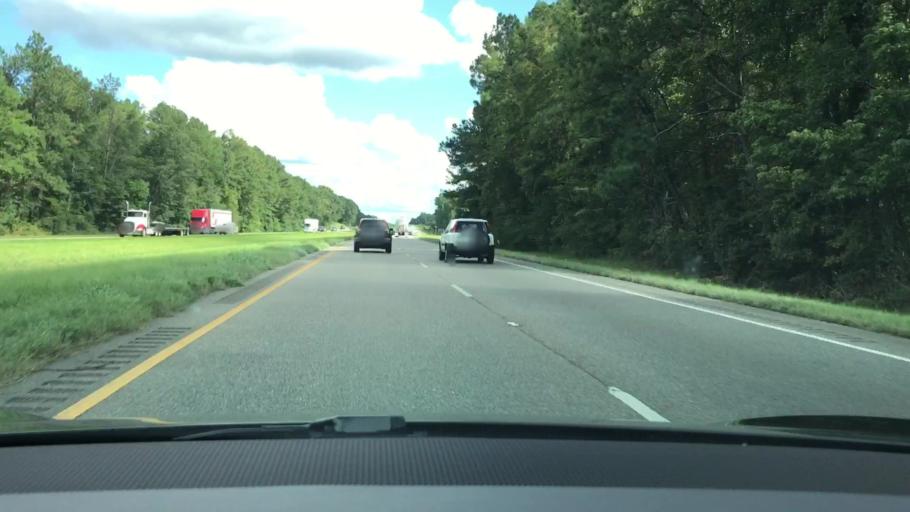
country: US
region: Alabama
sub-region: Montgomery County
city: Pike Road
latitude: 32.1345
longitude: -86.0882
